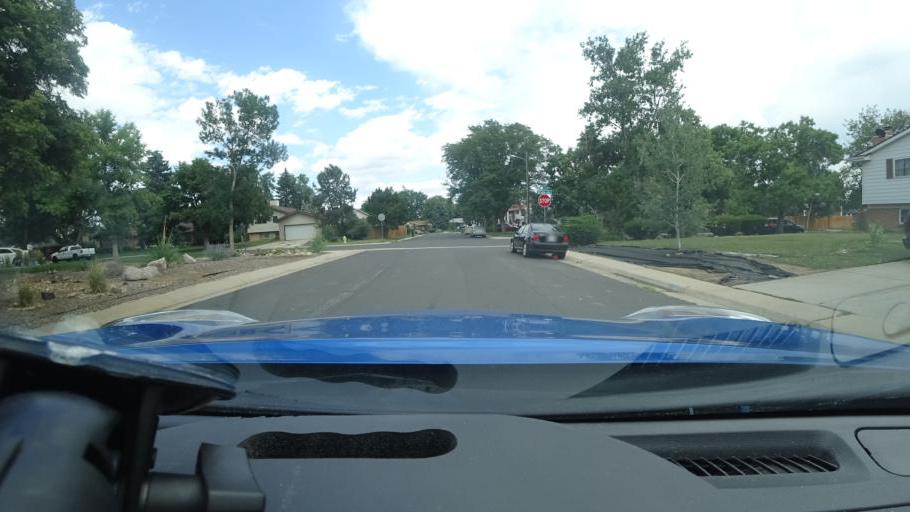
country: US
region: Colorado
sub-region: Adams County
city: Aurora
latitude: 39.7205
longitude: -104.8337
